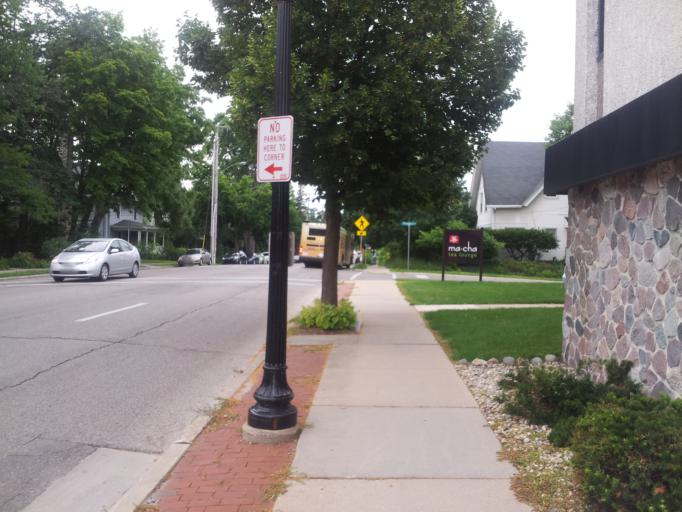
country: US
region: Wisconsin
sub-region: Dane County
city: Madison
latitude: 43.0640
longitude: -89.4187
